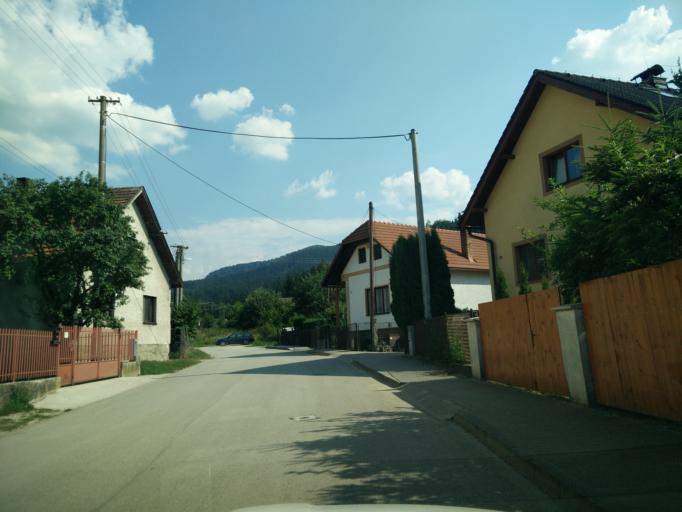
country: SK
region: Zilinsky
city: Rajec
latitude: 49.0970
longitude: 18.7125
